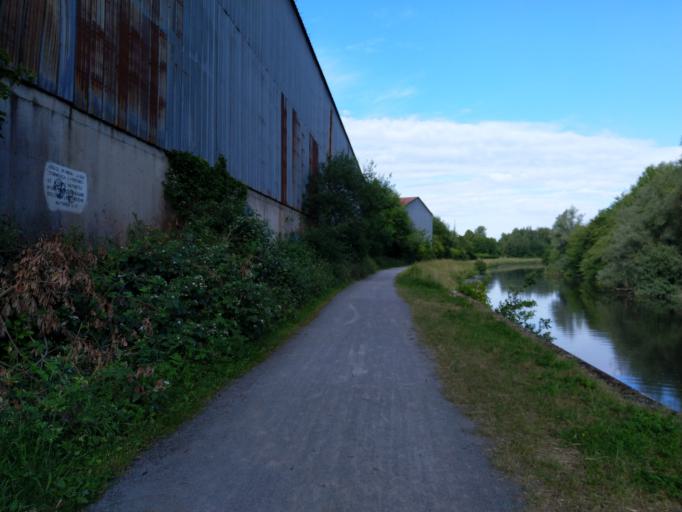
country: FR
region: Nord-Pas-de-Calais
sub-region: Departement du Nord
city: Jeumont
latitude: 50.2986
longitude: 4.0963
